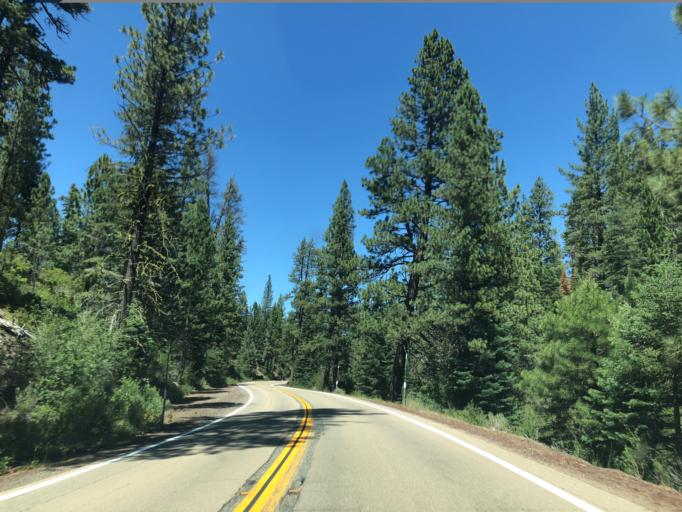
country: US
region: California
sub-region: Shasta County
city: Burney
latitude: 40.6466
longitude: -121.4647
